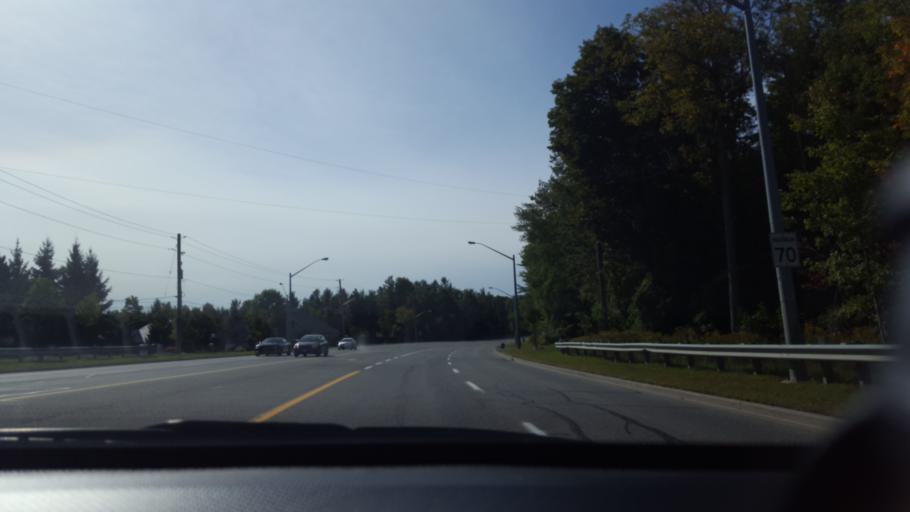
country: CA
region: Ontario
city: Newmarket
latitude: 44.0286
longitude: -79.4958
